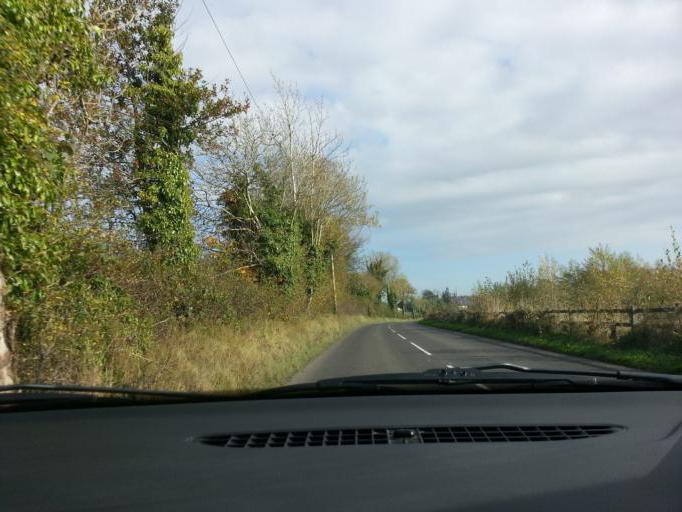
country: IE
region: Ulster
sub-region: County Monaghan
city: Clones
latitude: 54.2295
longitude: -7.2884
